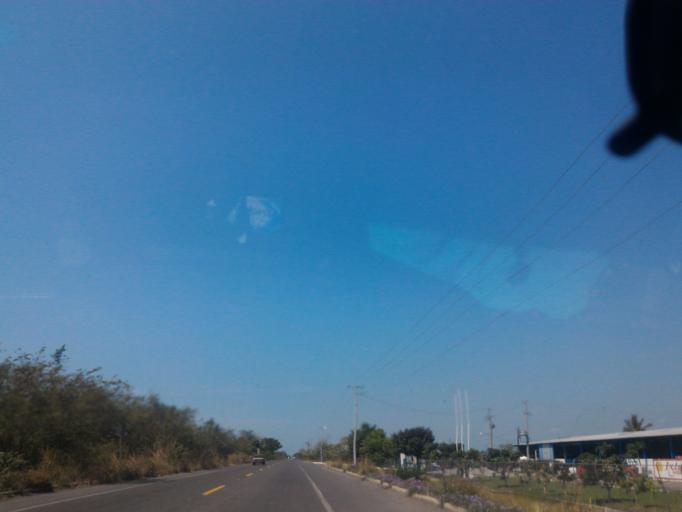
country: MX
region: Michoacan
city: Coahuayana Viejo
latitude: 18.7752
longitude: -103.7497
